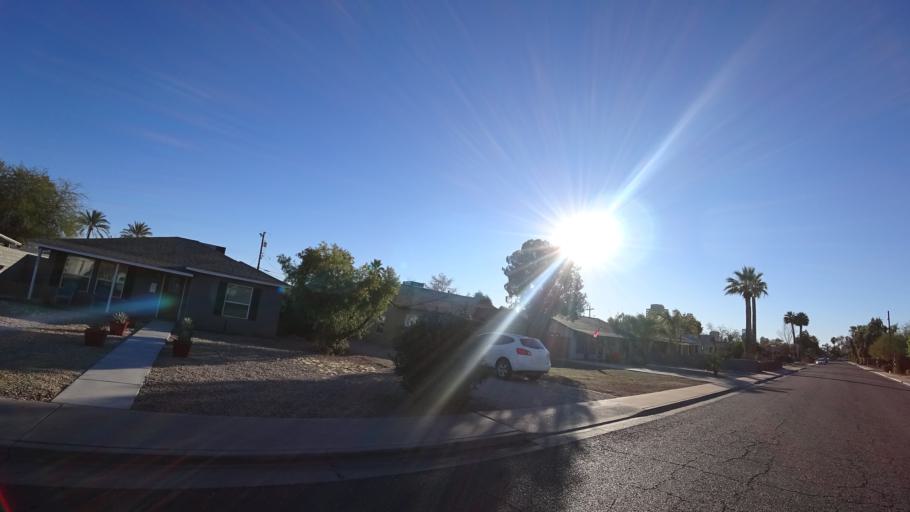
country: US
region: Arizona
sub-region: Maricopa County
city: Phoenix
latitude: 33.4902
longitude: -112.0533
